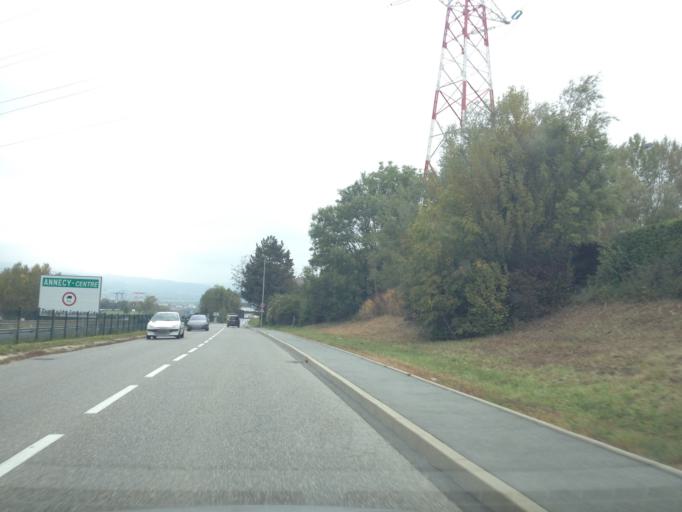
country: FR
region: Rhone-Alpes
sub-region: Departement de la Haute-Savoie
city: Seynod
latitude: 45.8884
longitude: 6.0840
